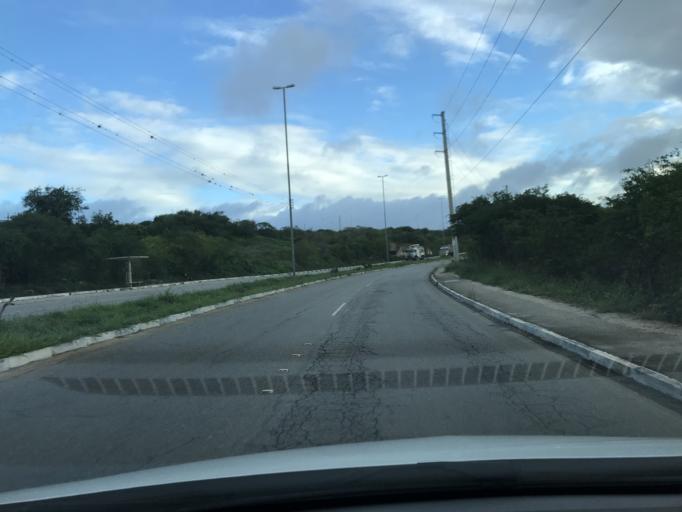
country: BR
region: Pernambuco
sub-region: Caruaru
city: Caruaru
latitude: -8.3037
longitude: -35.9404
